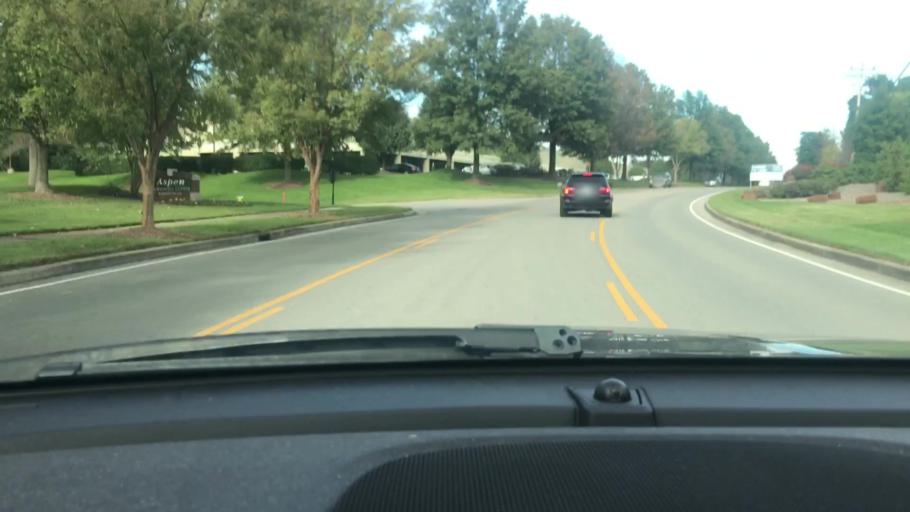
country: US
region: Tennessee
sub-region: Williamson County
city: Franklin
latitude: 35.9484
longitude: -86.8322
